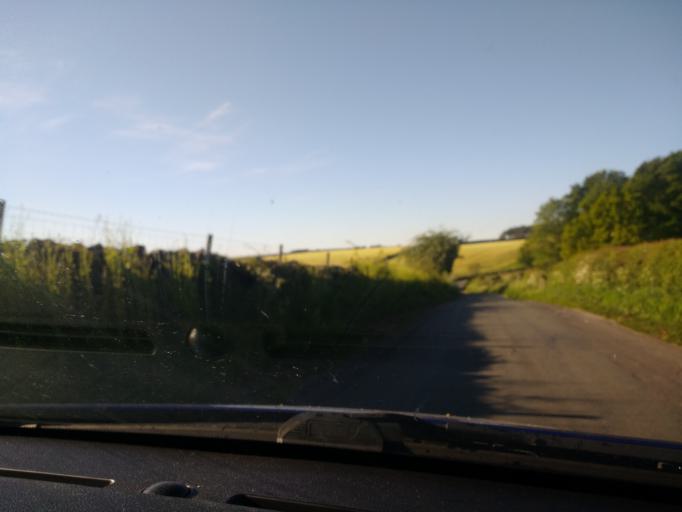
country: GB
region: England
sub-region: Cumbria
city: Appleby-in-Westmorland
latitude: 54.6703
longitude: -2.5946
